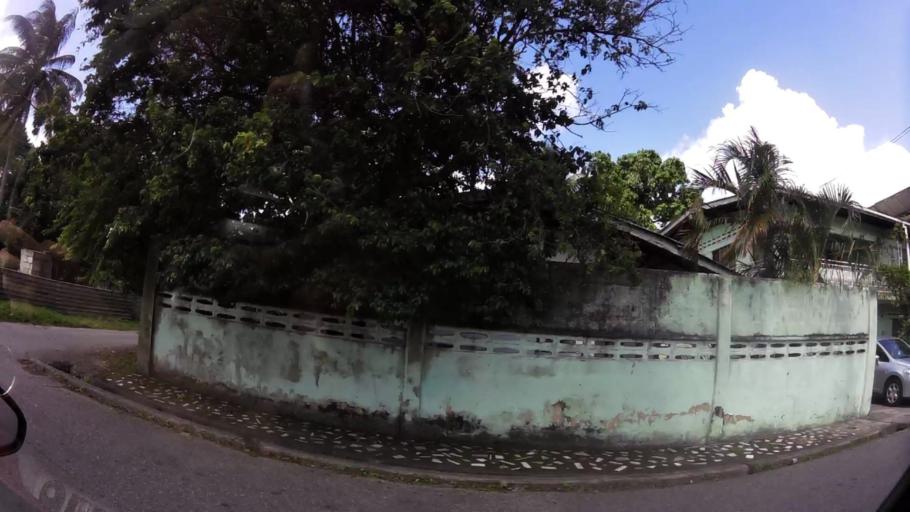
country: TT
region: Borough of Arima
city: Arima
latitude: 10.6310
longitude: -61.2768
